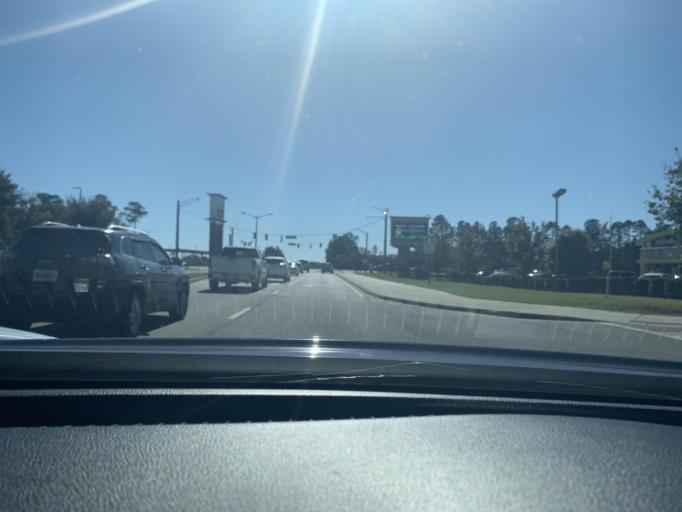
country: US
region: Georgia
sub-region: Chatham County
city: Pooler
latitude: 32.1418
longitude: -81.2473
